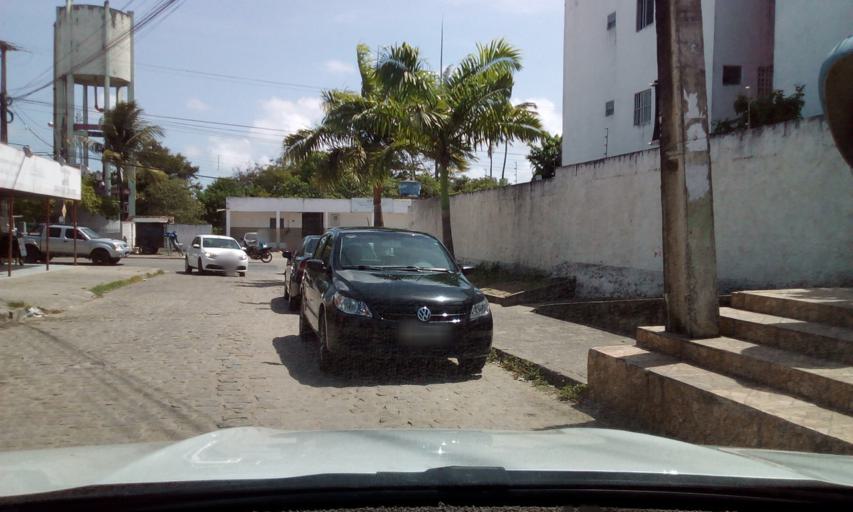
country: BR
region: Paraiba
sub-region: Joao Pessoa
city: Joao Pessoa
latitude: -7.0981
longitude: -34.8665
